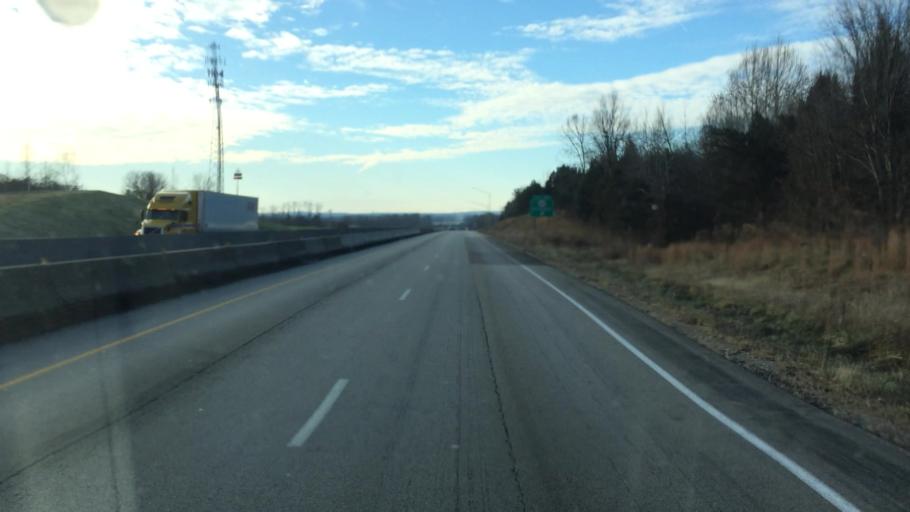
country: US
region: Kentucky
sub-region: Hardin County
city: Elizabethtown
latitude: 37.6040
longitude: -85.8672
